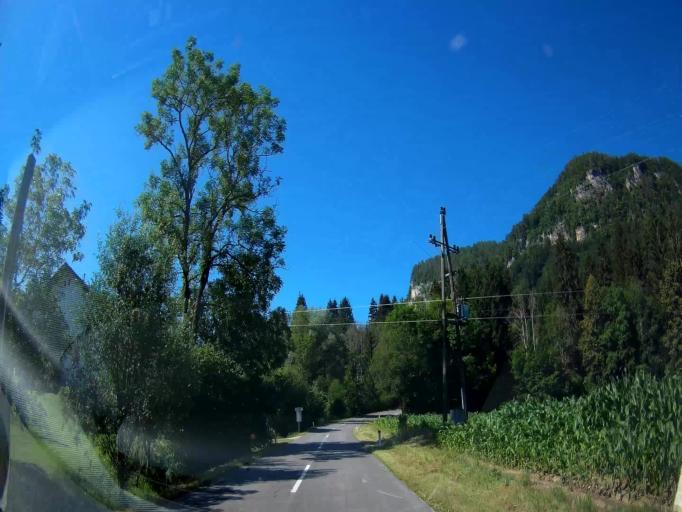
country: AT
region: Carinthia
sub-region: Politischer Bezirk Klagenfurt Land
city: Grafenstein
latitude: 46.5982
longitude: 14.4379
